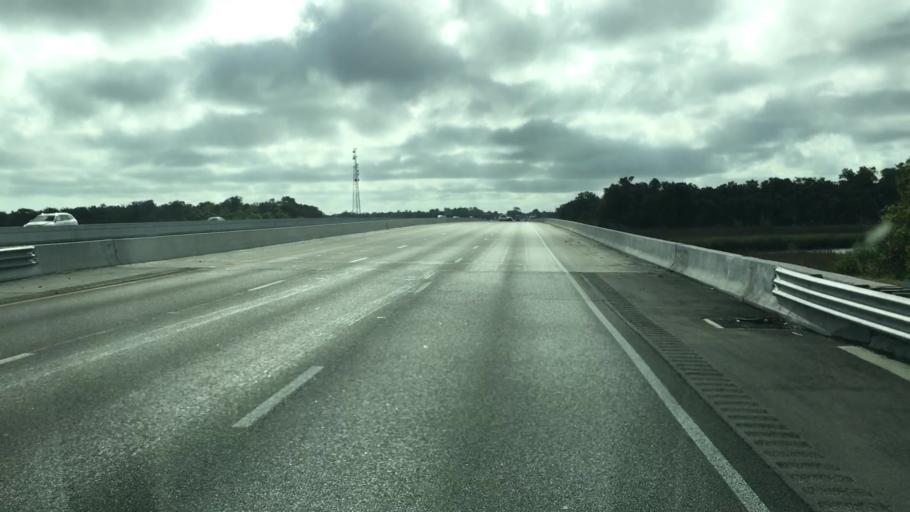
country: US
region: Florida
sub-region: Volusia County
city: Port Orange
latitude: 29.0923
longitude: -81.0221
